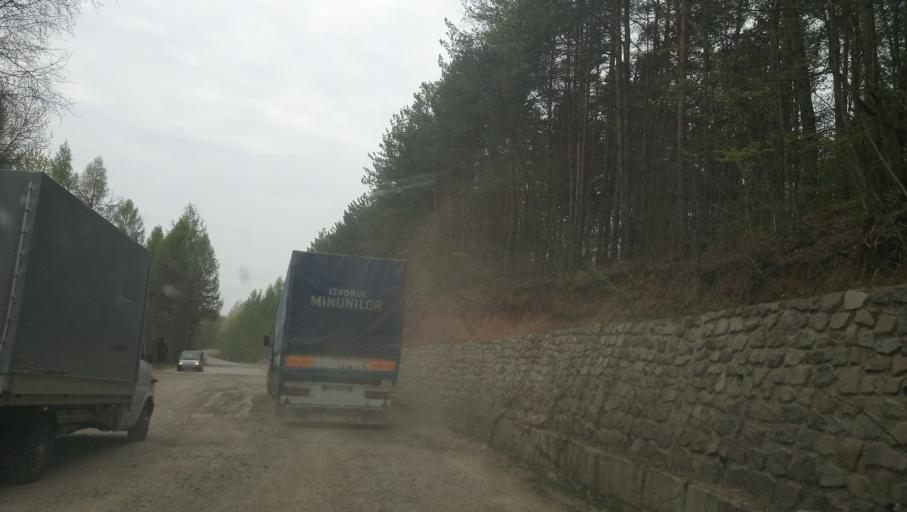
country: RO
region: Arad
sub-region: Comuna Varfurile
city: Varfurile
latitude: 46.3652
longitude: 22.5498
